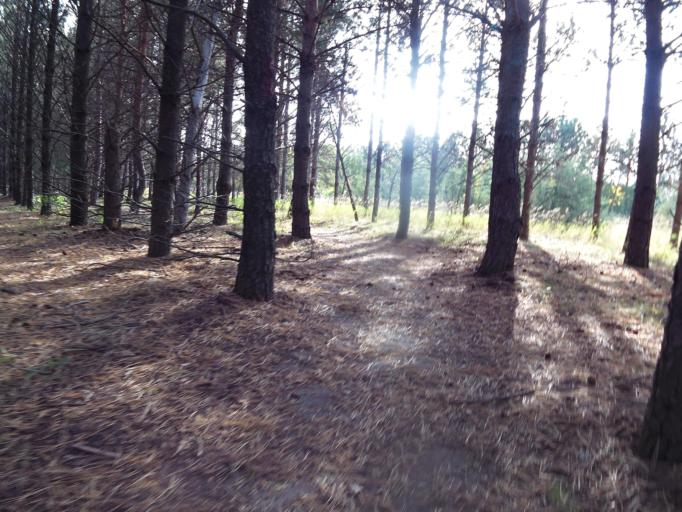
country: US
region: North Dakota
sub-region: Pembina County
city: Cavalier
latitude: 48.7805
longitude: -97.7523
